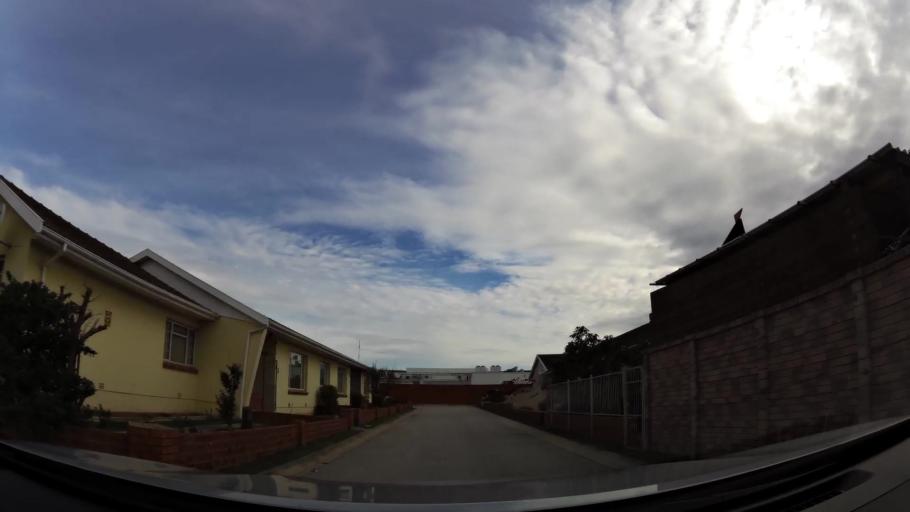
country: ZA
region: Eastern Cape
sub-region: Nelson Mandela Bay Metropolitan Municipality
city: Port Elizabeth
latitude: -33.9425
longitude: 25.5129
